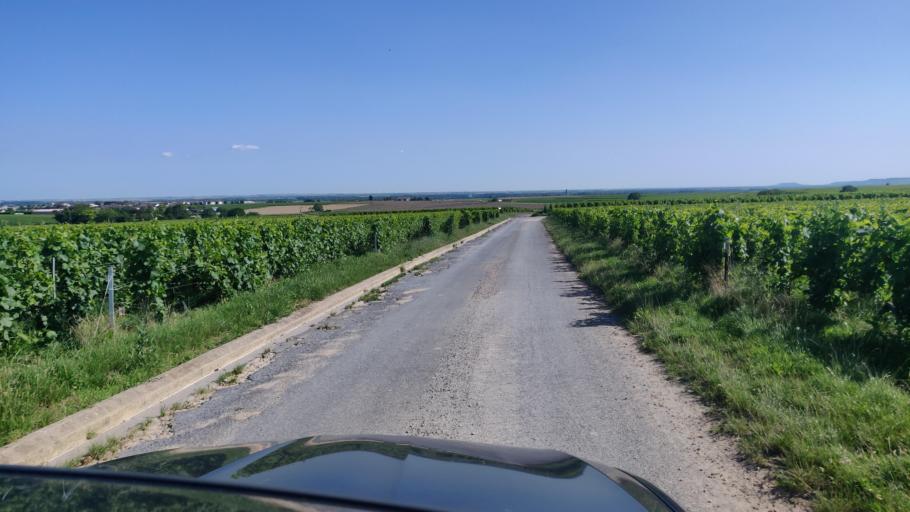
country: FR
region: Champagne-Ardenne
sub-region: Departement de la Marne
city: Tours-sur-Marne
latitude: 49.0872
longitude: 4.1352
